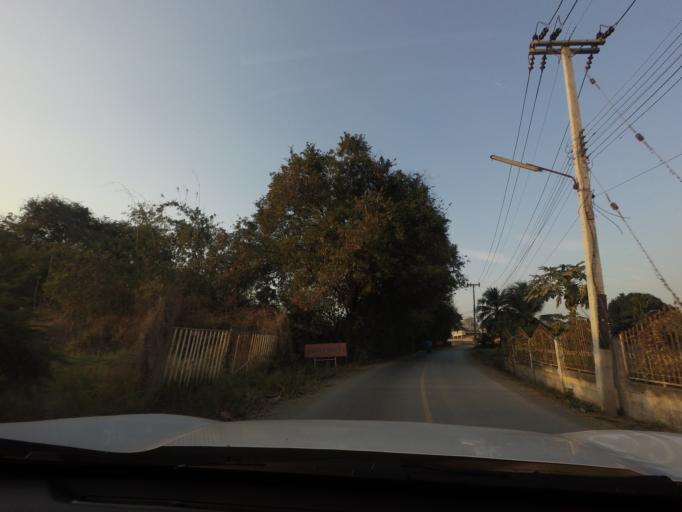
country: TH
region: Nakhon Ratchasima
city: Pak Chong
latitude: 14.6473
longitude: 101.4202
